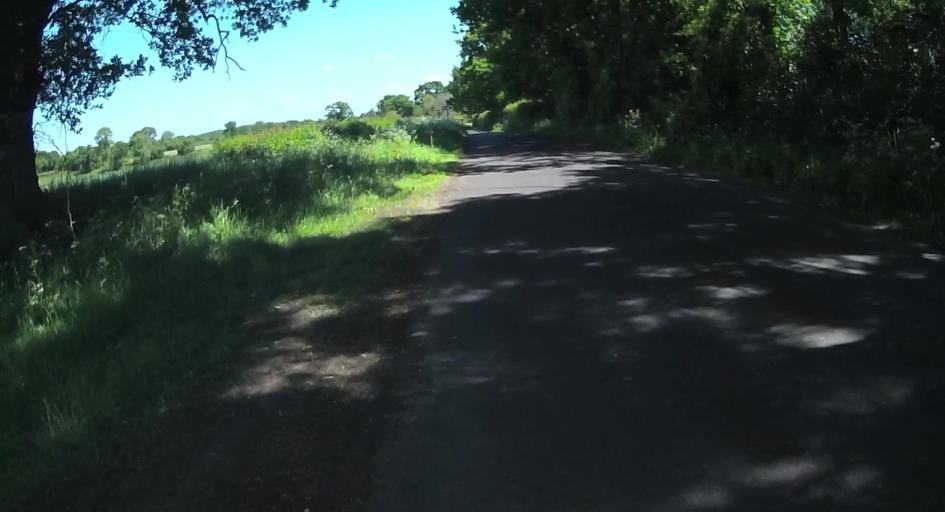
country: GB
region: England
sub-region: West Berkshire
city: Stratfield Mortimer
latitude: 51.3518
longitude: -1.0308
